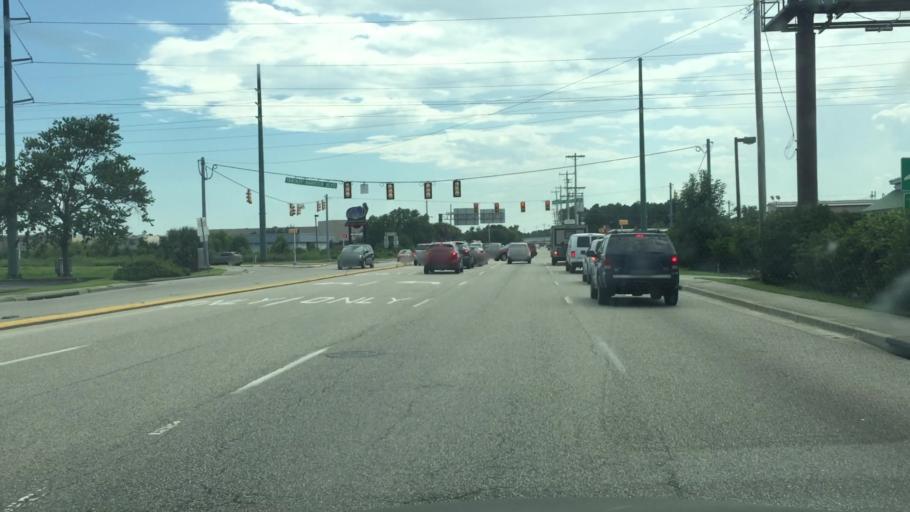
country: US
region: South Carolina
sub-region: Horry County
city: Forestbrook
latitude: 33.7194
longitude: -78.9313
